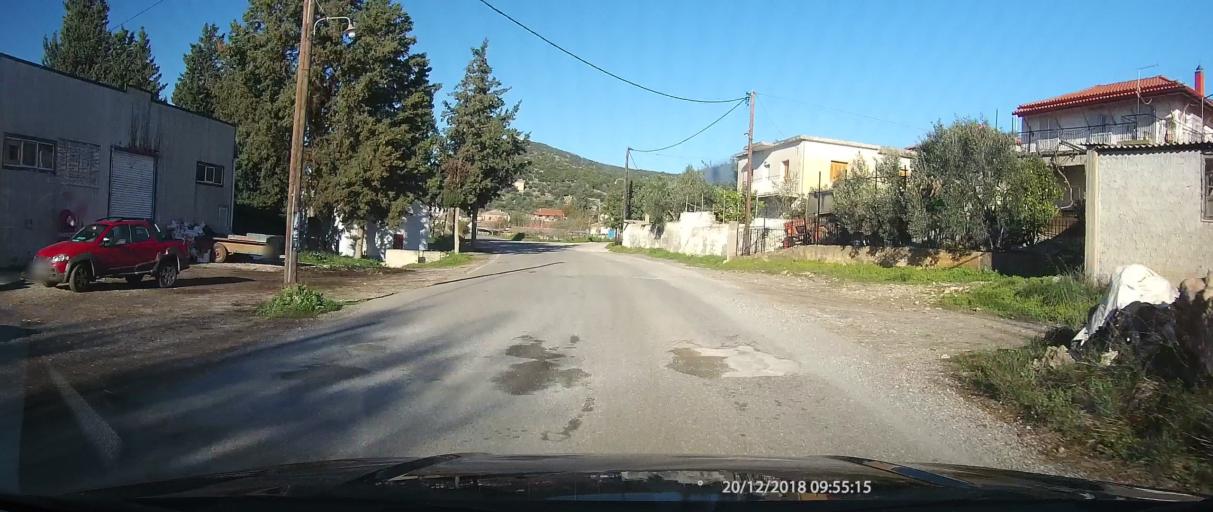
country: GR
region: Peloponnese
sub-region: Nomos Lakonias
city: Yerakion
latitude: 37.0236
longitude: 22.6249
